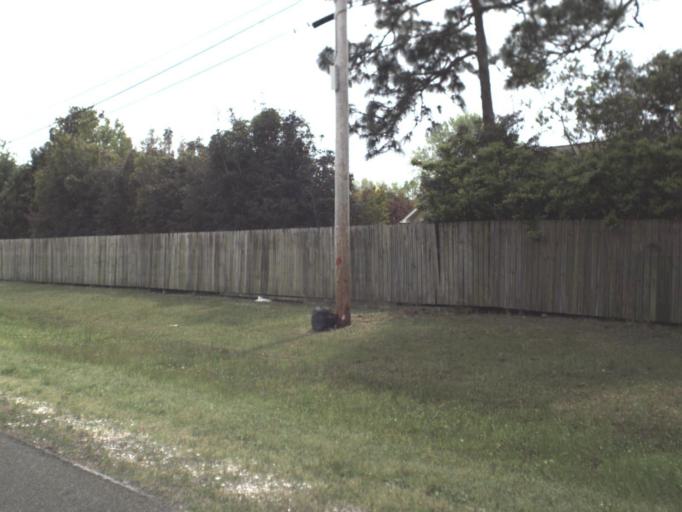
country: US
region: Florida
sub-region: Santa Rosa County
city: Navarre
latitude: 30.4096
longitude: -86.8317
